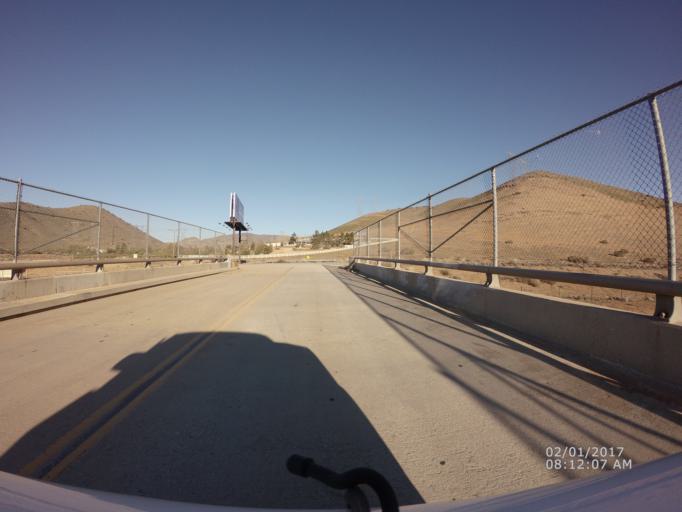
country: US
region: California
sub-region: Los Angeles County
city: Vincent
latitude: 34.5024
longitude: -118.1188
